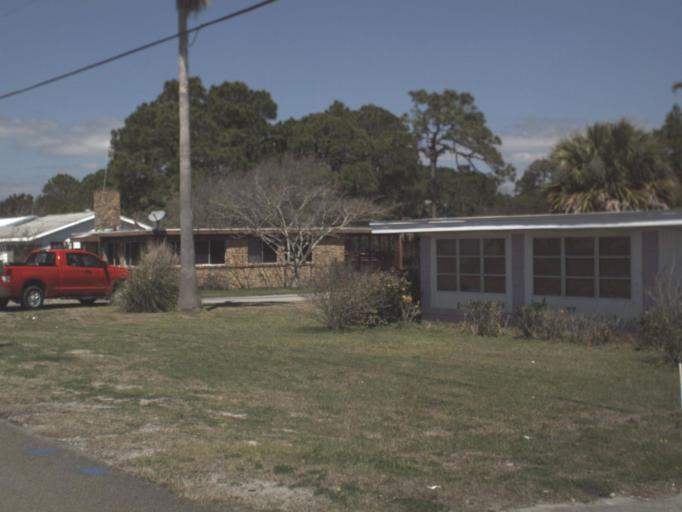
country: US
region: Florida
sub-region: Bay County
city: Mexico Beach
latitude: 29.8934
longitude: -85.3589
